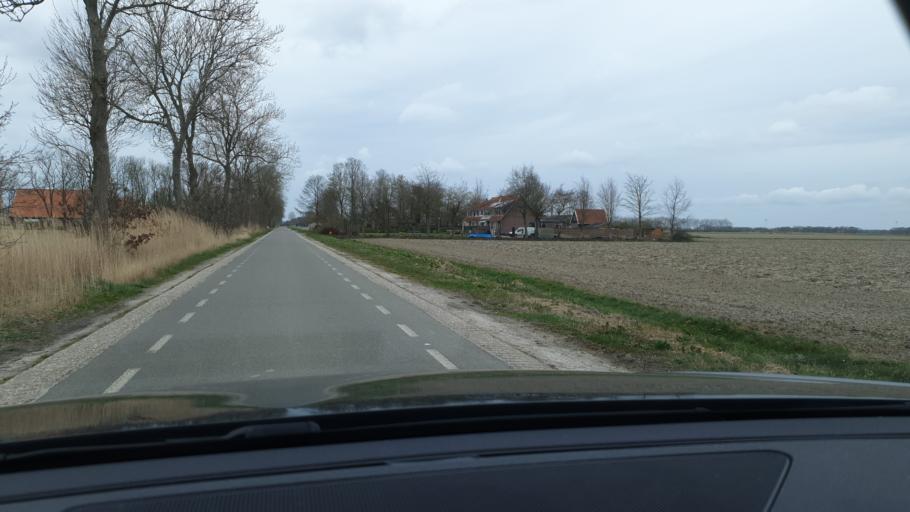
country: NL
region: Flevoland
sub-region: Gemeente Noordoostpolder
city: Emmeloord
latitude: 52.7089
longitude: 5.6998
